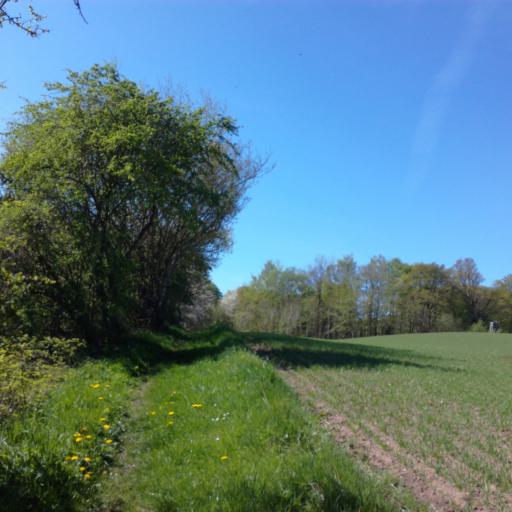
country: DK
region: South Denmark
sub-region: Vejle Kommune
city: Brejning
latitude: 55.6155
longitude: 9.7069
